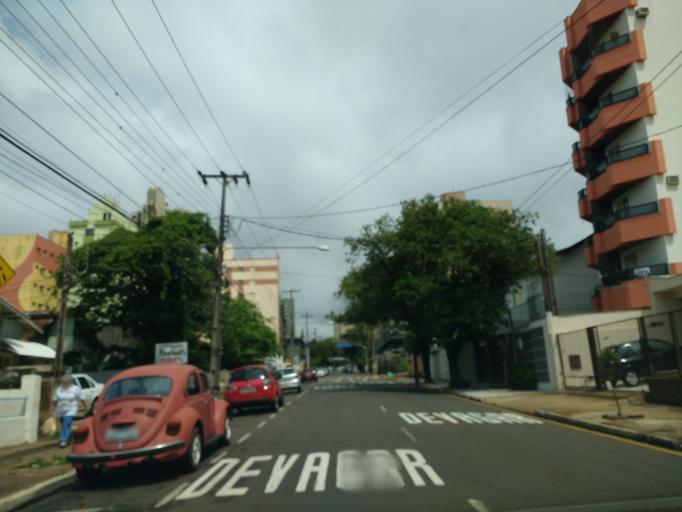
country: BR
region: Parana
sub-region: Londrina
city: Londrina
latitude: -23.3218
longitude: -51.1650
